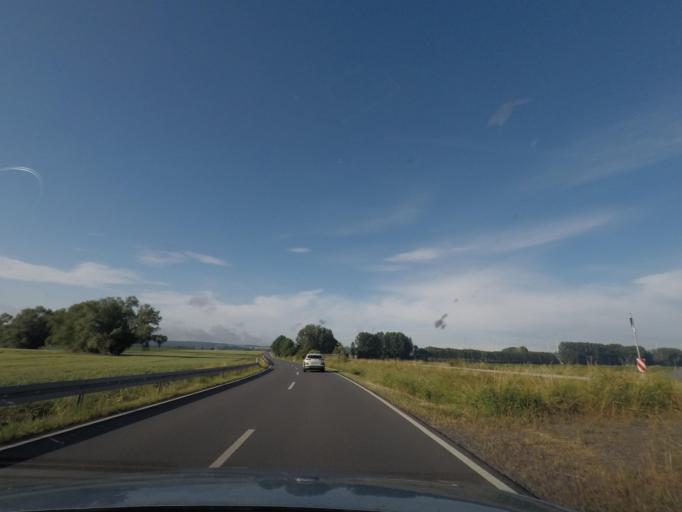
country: DE
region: Saxony-Anhalt
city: Huy-Neinstedt
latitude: 52.0056
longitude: 10.8952
